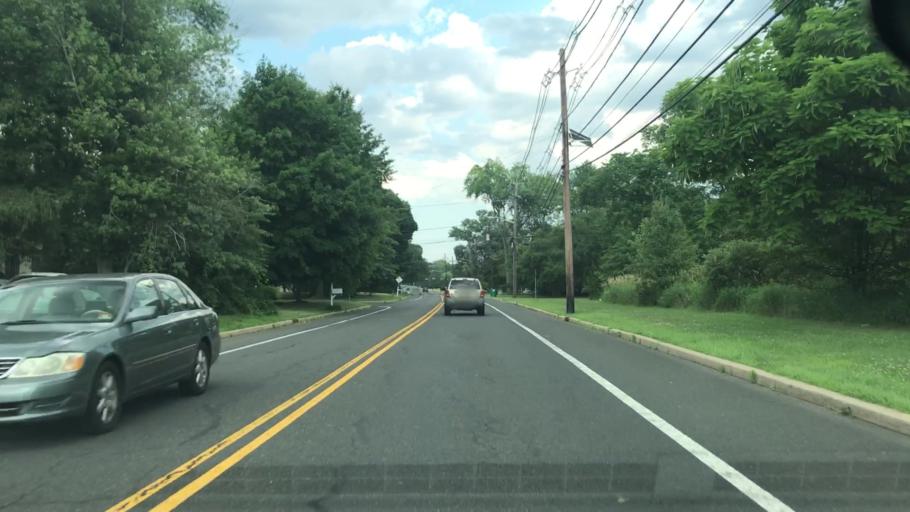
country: US
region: New Jersey
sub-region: Somerset County
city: Bradley Gardens
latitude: 40.5548
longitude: -74.6695
